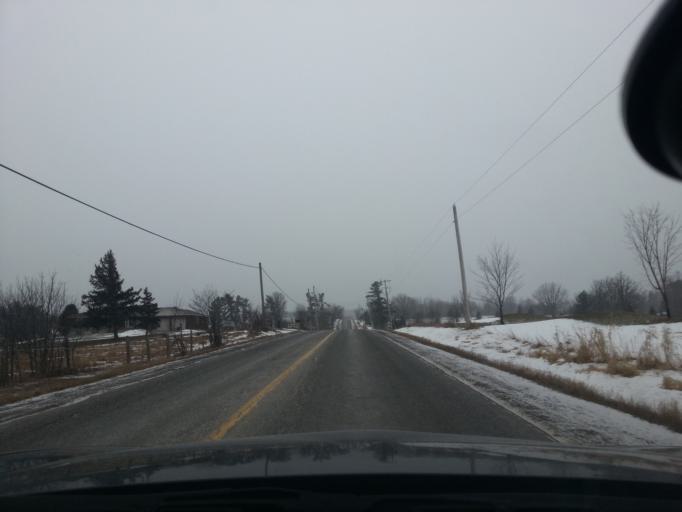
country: CA
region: Ontario
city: Arnprior
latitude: 45.3251
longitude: -76.2931
